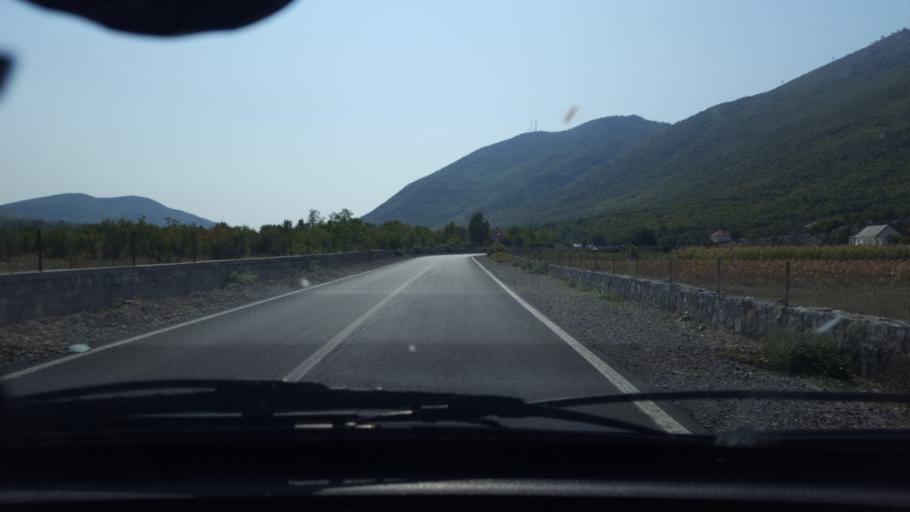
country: AL
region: Shkoder
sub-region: Rrethi i Malesia e Madhe
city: Kastrat
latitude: 42.4063
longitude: 19.4983
